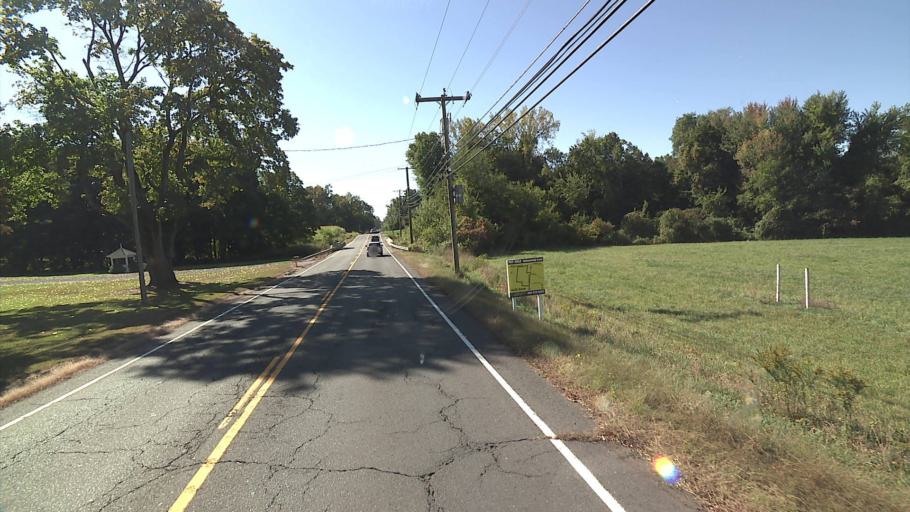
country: US
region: Connecticut
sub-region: Tolland County
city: Ellington
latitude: 41.9154
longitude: -72.4536
